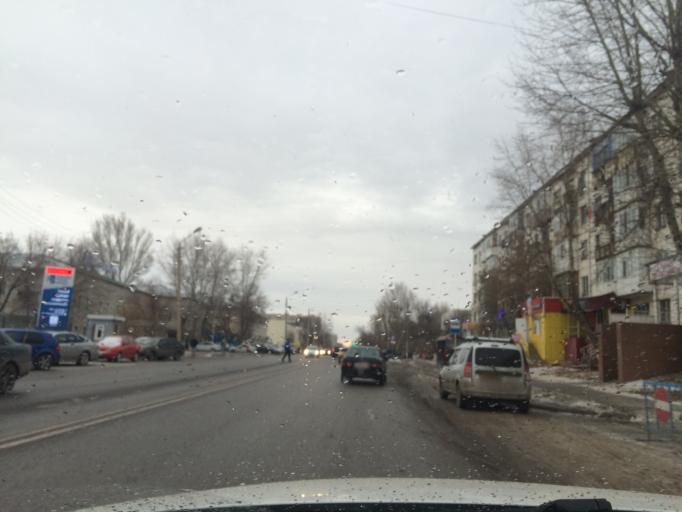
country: KZ
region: Astana Qalasy
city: Astana
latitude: 51.1861
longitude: 71.4213
